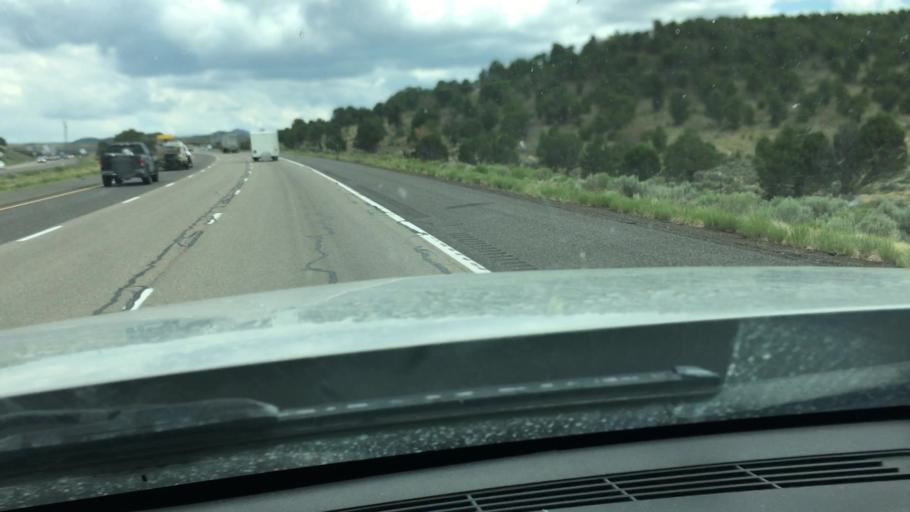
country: US
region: Utah
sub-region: Beaver County
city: Beaver
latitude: 38.1636
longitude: -112.6201
